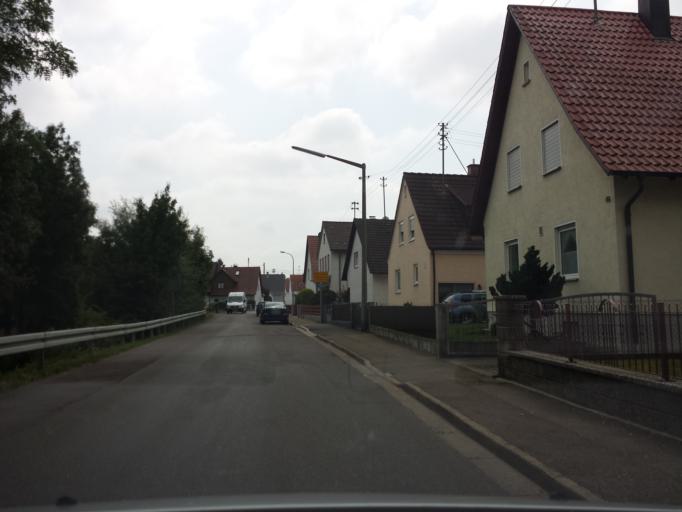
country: DE
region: Bavaria
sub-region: Swabia
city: Wasserburg
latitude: 48.4421
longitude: 10.2697
